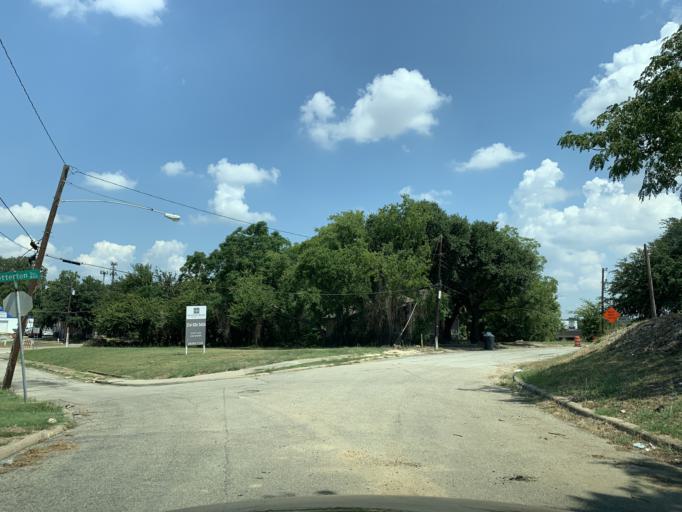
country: US
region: Texas
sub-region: Dallas County
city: Dallas
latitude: 32.7476
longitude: -96.8118
